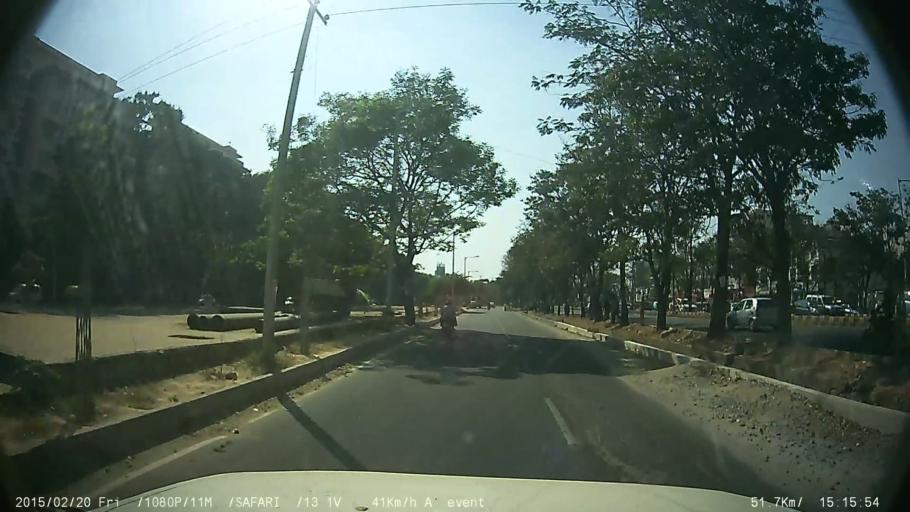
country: IN
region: Karnataka
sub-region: Bangalore Urban
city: Bangalore
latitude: 12.9165
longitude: 77.6305
